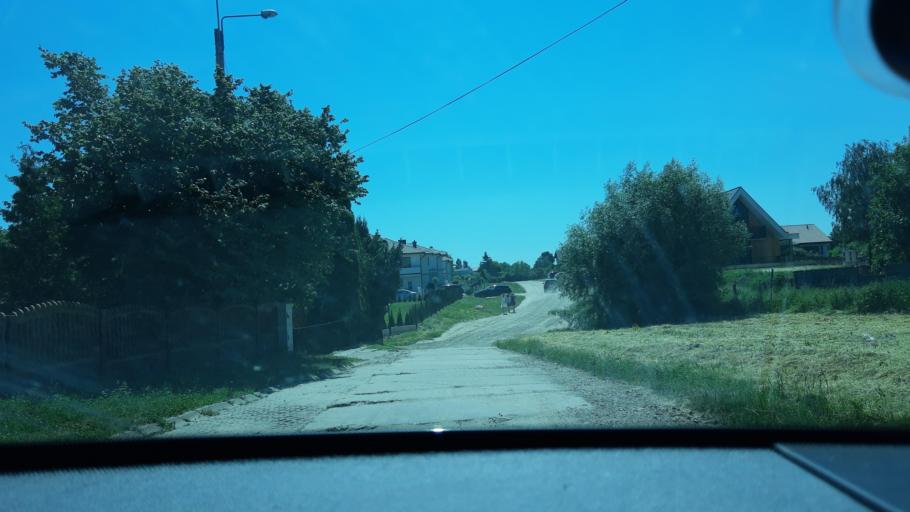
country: PL
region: Lodz Voivodeship
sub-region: Powiat sieradzki
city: Sieradz
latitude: 51.5861
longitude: 18.7332
